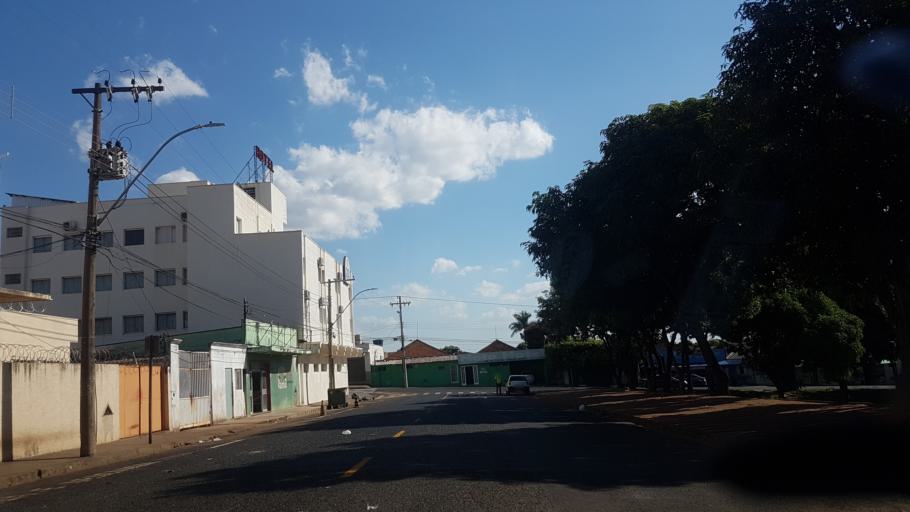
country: BR
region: Minas Gerais
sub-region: Uberlandia
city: Uberlandia
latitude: -18.9063
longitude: -48.2855
